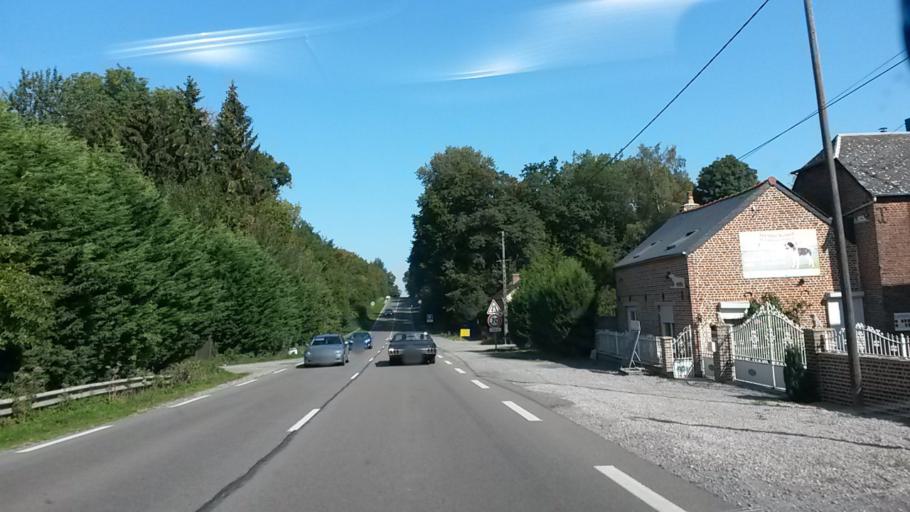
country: FR
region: Nord-Pas-de-Calais
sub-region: Departement du Nord
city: Hautmont
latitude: 50.1922
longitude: 3.9513
